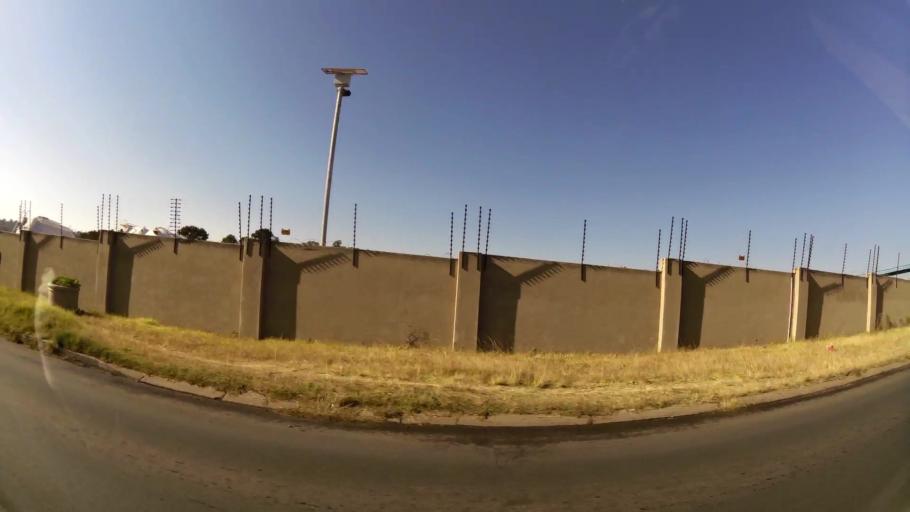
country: ZA
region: Gauteng
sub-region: City of Johannesburg Metropolitan Municipality
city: Modderfontein
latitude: -26.0670
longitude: 28.1947
